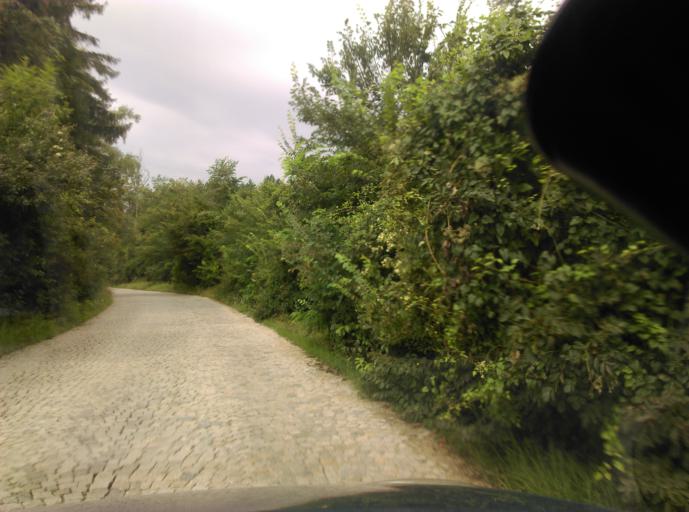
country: BG
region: Sofia-Capital
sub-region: Stolichna Obshtina
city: Sofia
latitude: 42.6068
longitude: 23.3954
